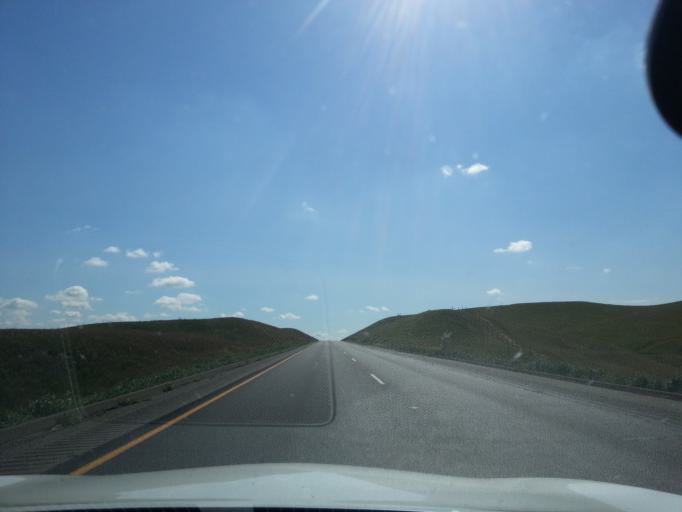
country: US
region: California
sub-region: Fresno County
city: Coalinga
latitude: 36.3248
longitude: -120.2953
